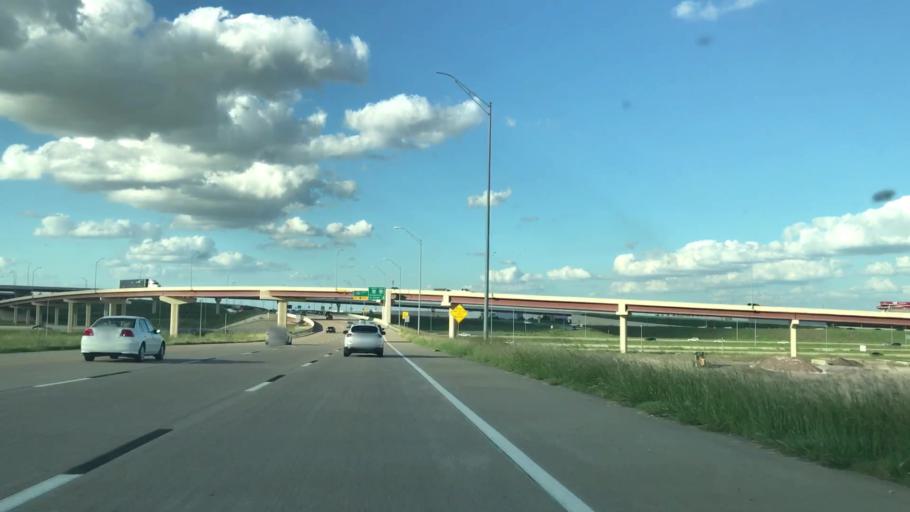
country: US
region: Texas
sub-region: Dallas County
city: Coppell
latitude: 32.9295
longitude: -97.0394
